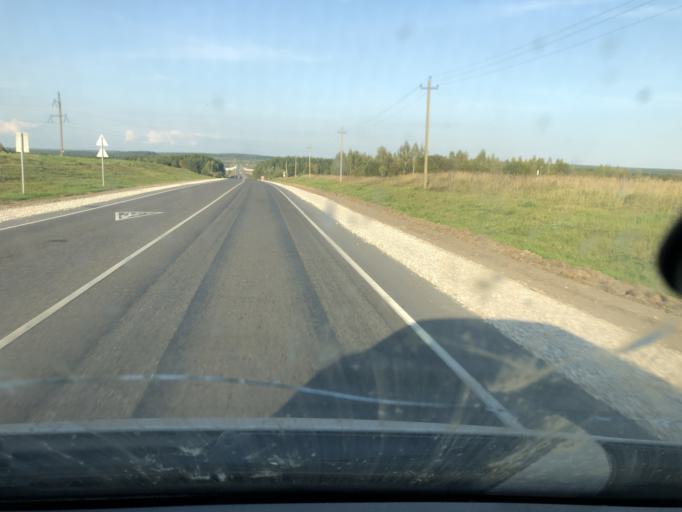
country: RU
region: Kaluga
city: Peremyshl'
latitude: 54.2796
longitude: 36.1464
